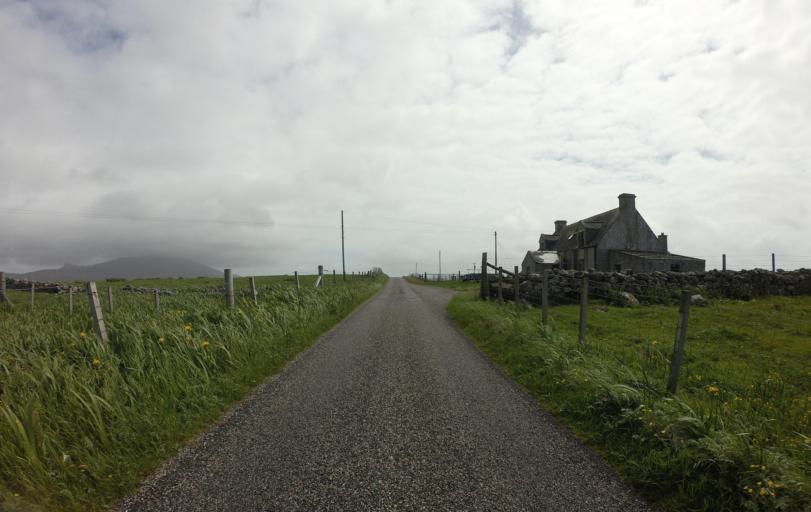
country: GB
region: Scotland
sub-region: Eilean Siar
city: Isle of South Uist
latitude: 57.2750
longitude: -7.4085
